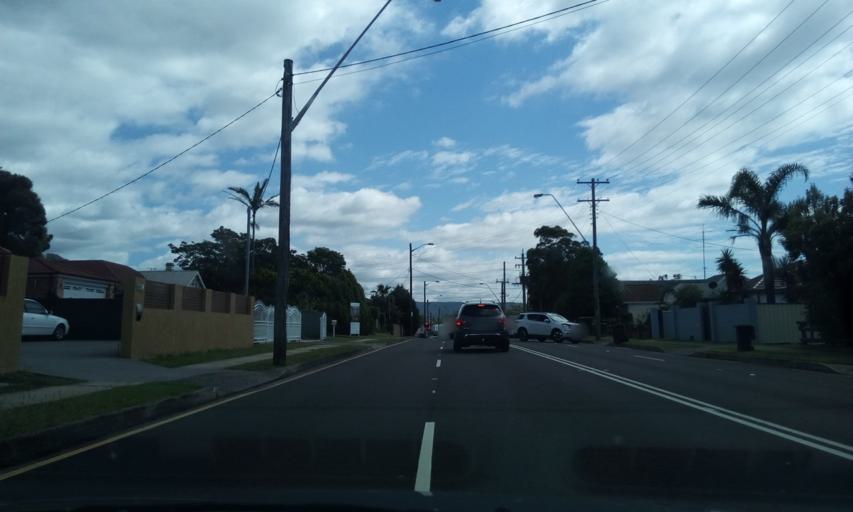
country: AU
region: New South Wales
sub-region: Wollongong
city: Corrimal
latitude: -34.3843
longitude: 150.8947
